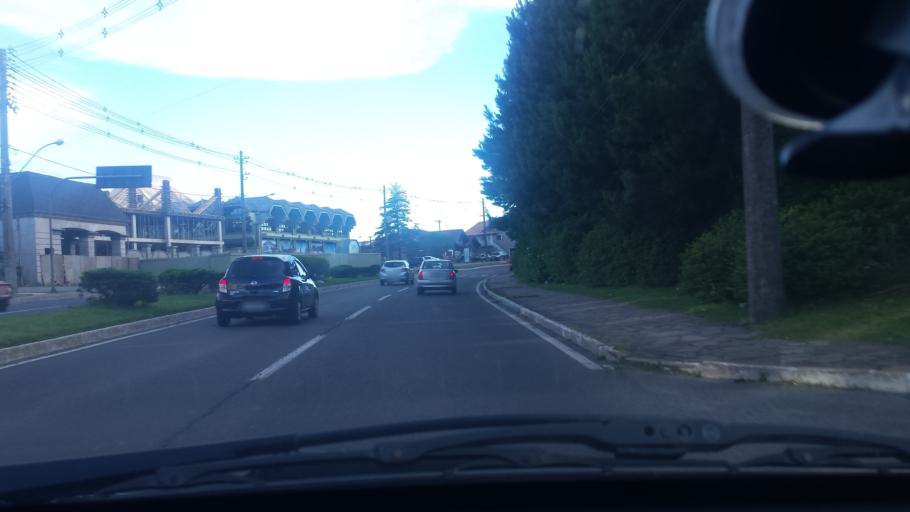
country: BR
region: Rio Grande do Sul
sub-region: Canela
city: Canela
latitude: -29.3754
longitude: -50.8646
